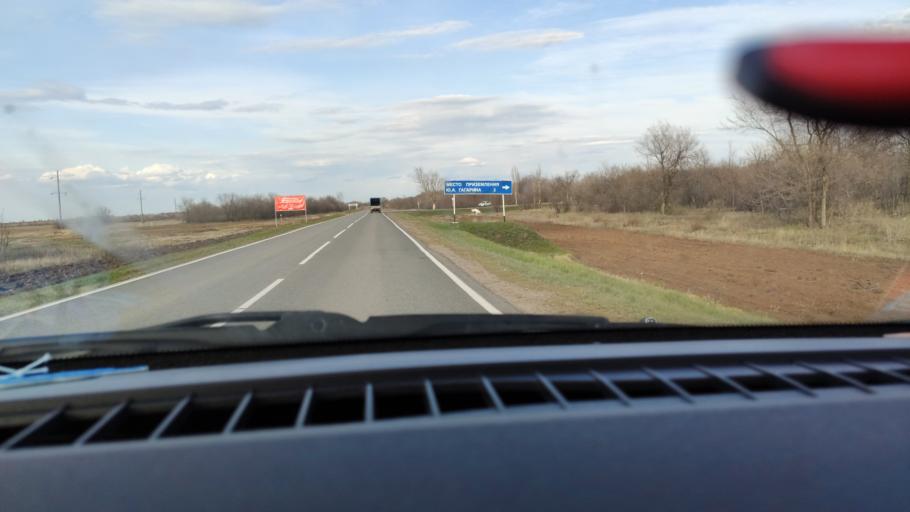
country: RU
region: Saratov
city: Privolzhskiy
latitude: 51.2845
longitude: 45.9664
